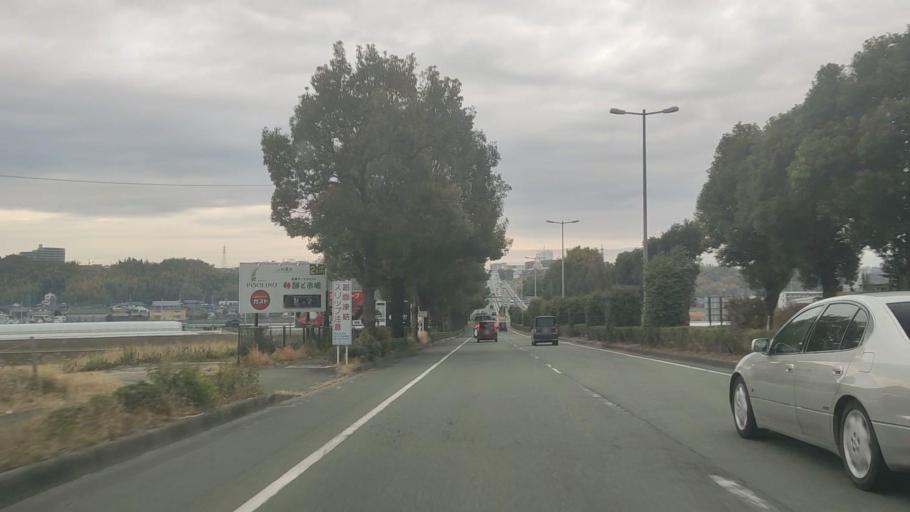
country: JP
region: Kumamoto
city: Ozu
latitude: 32.8439
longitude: 130.7810
